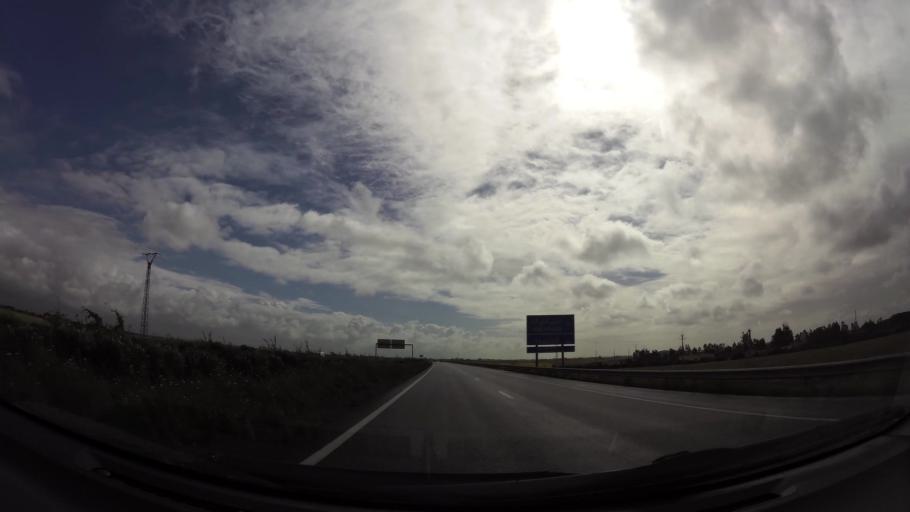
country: MA
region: Grand Casablanca
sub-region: Nouaceur
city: Dar Bouazza
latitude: 33.3465
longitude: -8.0043
